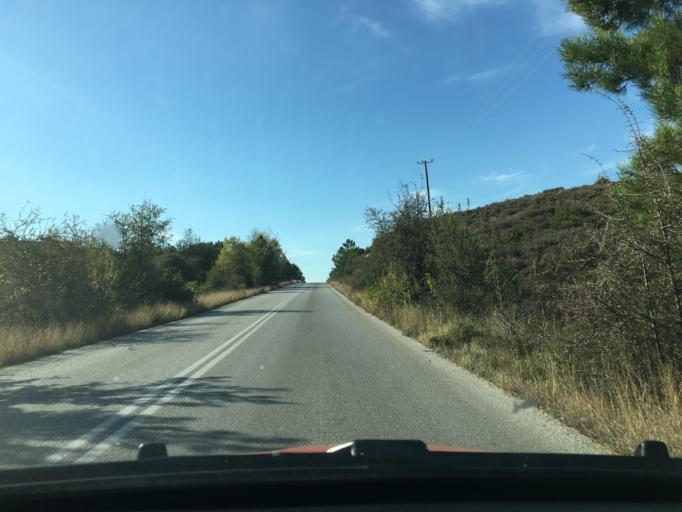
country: GR
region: Central Macedonia
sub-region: Nomos Chalkidikis
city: Megali Panagia
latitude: 40.3825
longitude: 23.7372
